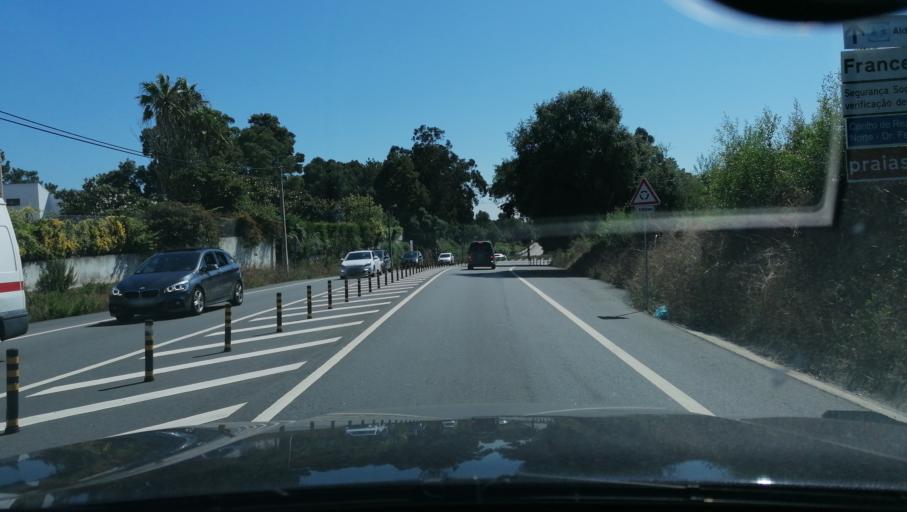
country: PT
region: Porto
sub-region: Vila Nova de Gaia
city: Gulpilhares
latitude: 41.0838
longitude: -8.6341
